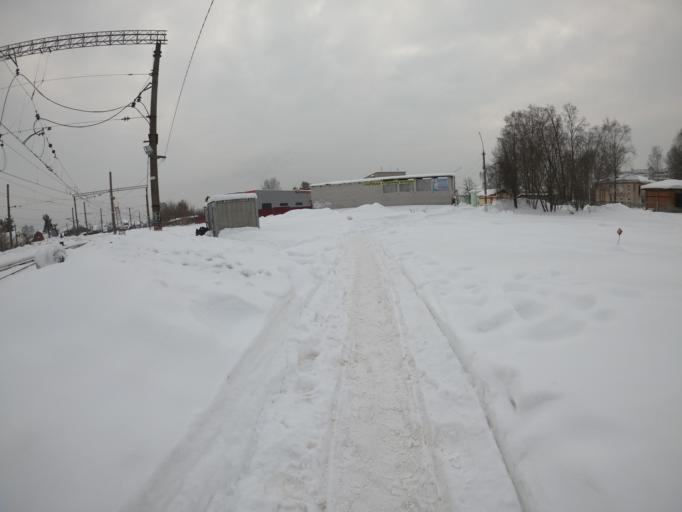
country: RU
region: Moskovskaya
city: Elektrogorsk
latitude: 55.8817
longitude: 38.7877
